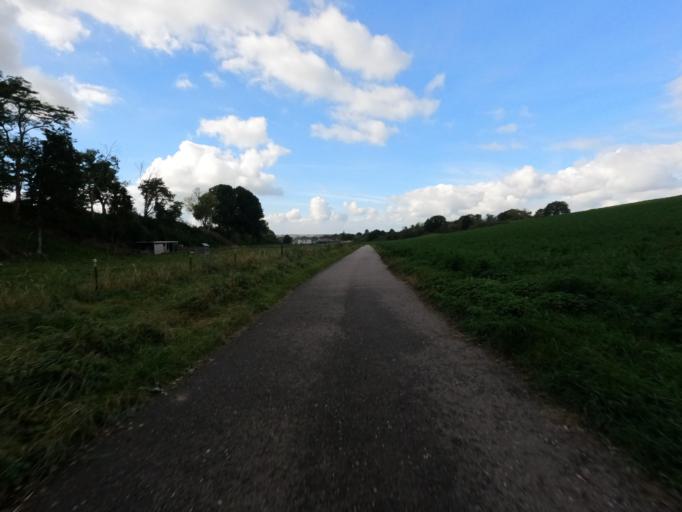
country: DE
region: North Rhine-Westphalia
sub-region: Regierungsbezirk Koln
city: Linnich
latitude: 51.0035
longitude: 6.2904
